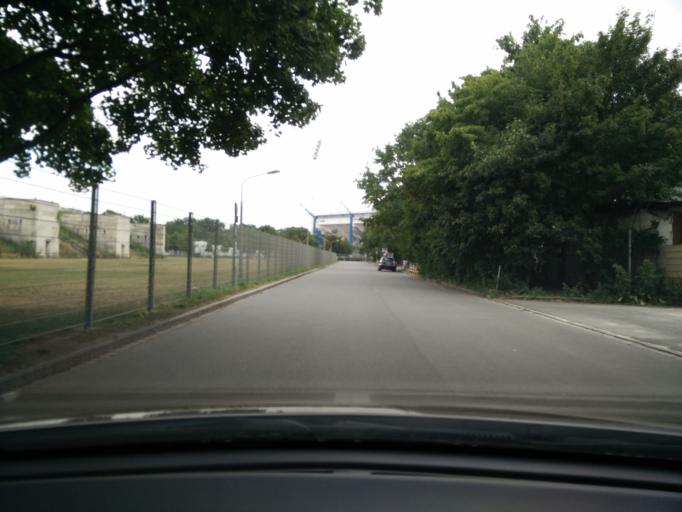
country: DE
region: Bavaria
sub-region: Regierungsbezirk Mittelfranken
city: Nuernberg
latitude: 49.4285
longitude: 11.1225
